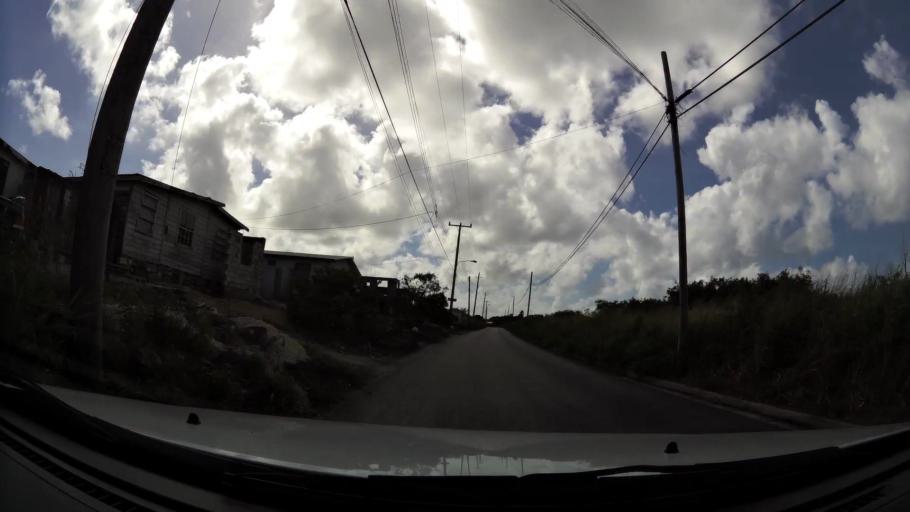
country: BB
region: Saint Lucy
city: Checker Hall
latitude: 13.2926
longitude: -59.6414
